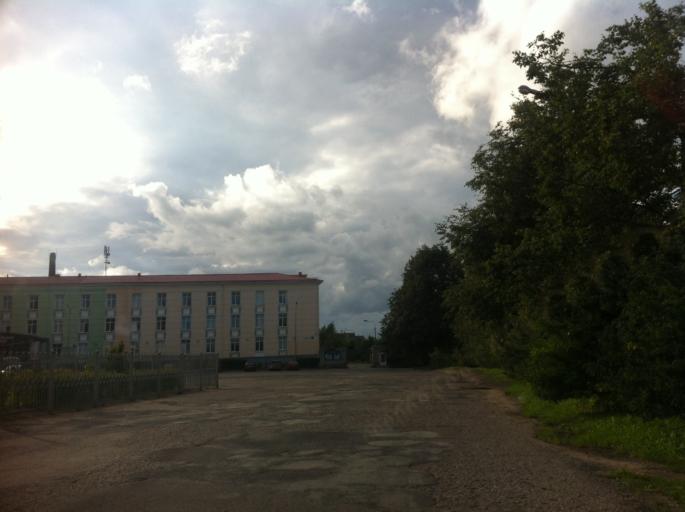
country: RU
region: Pskov
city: Pskov
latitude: 57.8259
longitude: 28.3185
